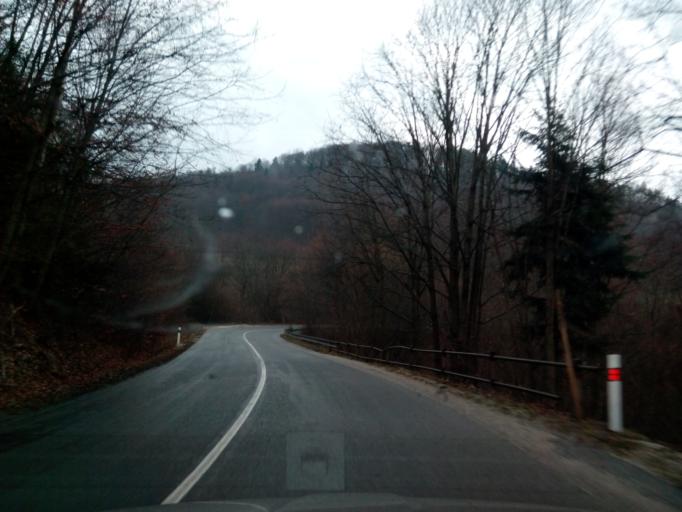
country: SK
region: Kosicky
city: Gelnica
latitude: 48.8384
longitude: 21.0465
